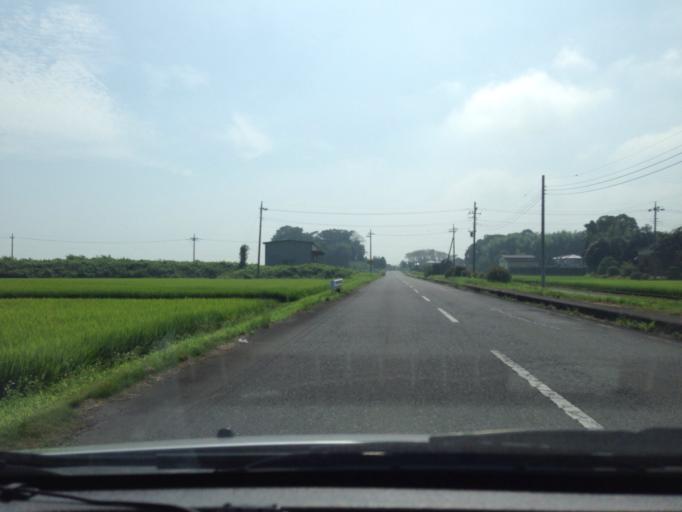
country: JP
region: Ibaraki
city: Inashiki
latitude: 36.0241
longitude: 140.3129
